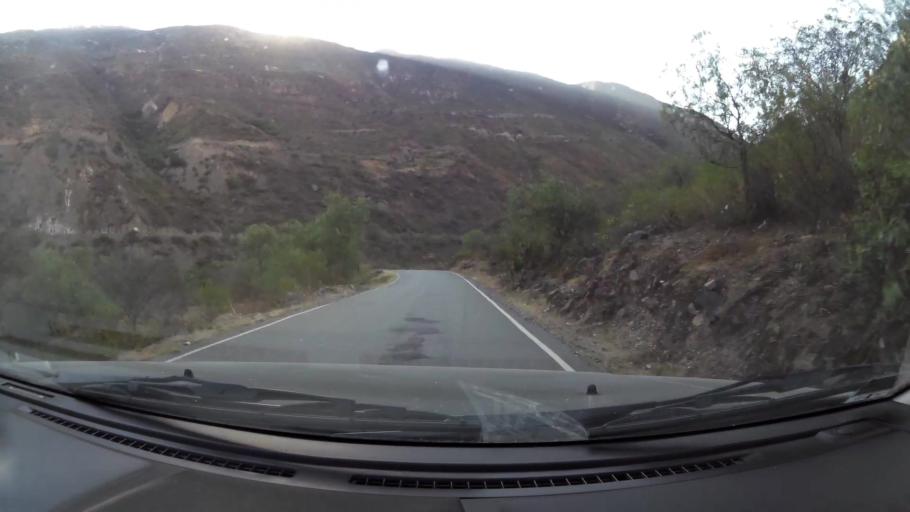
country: PE
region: Huancavelica
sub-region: Provincia de Churcampa
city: La Esmeralda
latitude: -12.5854
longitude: -74.6945
